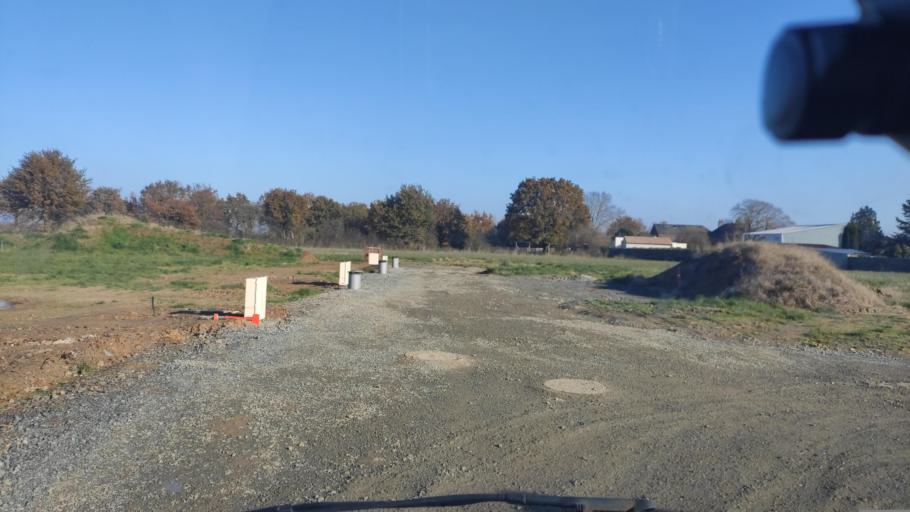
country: FR
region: Pays de la Loire
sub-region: Departement de la Vendee
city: Les Essarts
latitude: 46.7710
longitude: -1.2410
